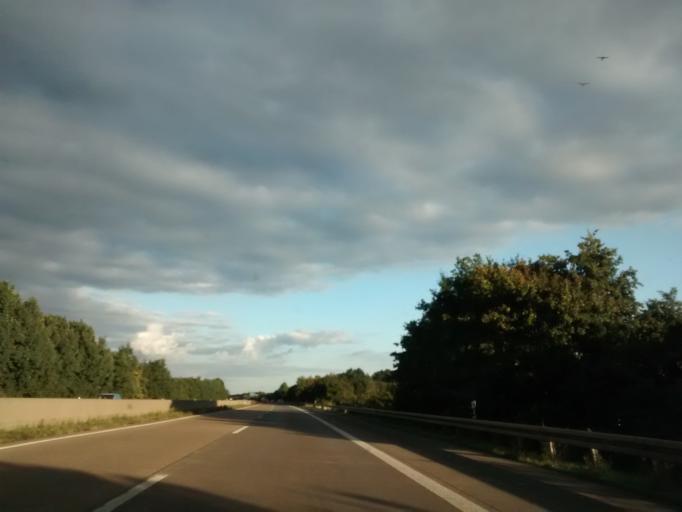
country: DE
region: North Rhine-Westphalia
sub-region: Regierungsbezirk Munster
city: Dreierwalde
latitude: 52.2949
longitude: 7.5154
